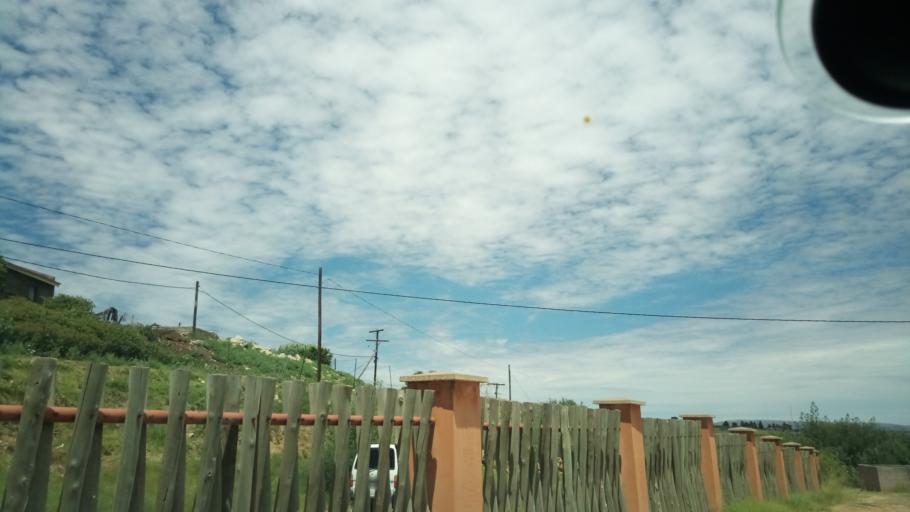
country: LS
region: Maseru
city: Maseru
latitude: -29.3463
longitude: 27.6640
